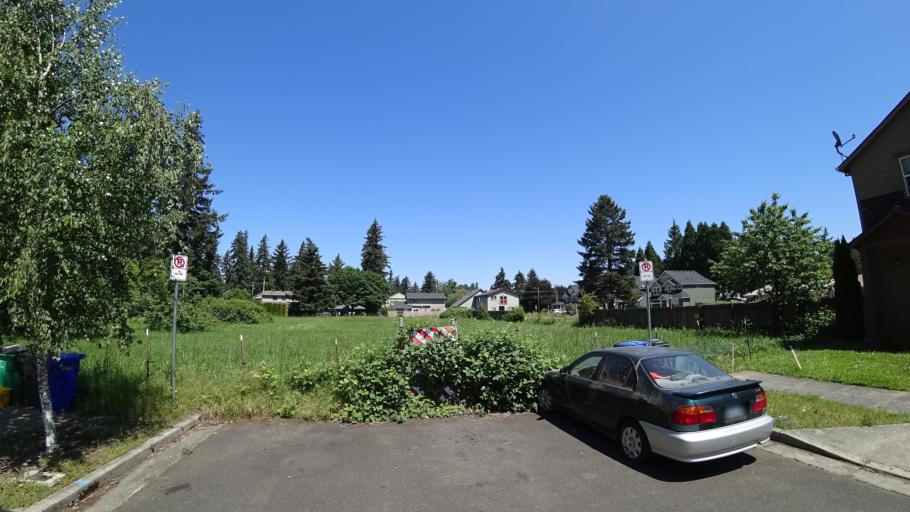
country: US
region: Oregon
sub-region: Clackamas County
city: Happy Valley
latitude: 45.4789
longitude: -122.5258
